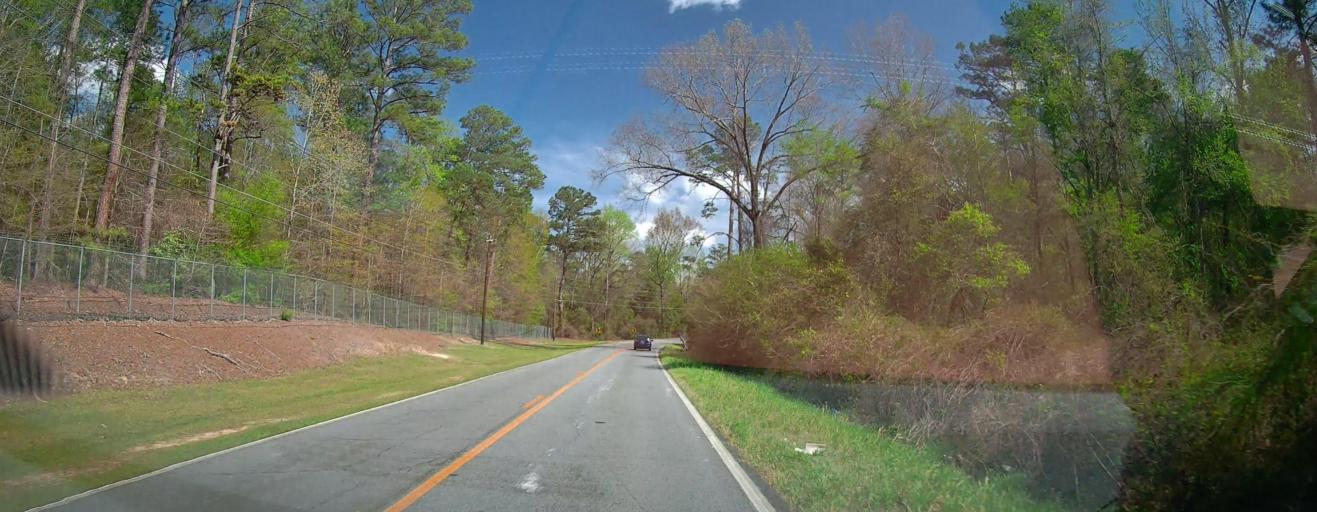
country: US
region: Georgia
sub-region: Bibb County
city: Macon
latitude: 32.8149
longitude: -83.5431
